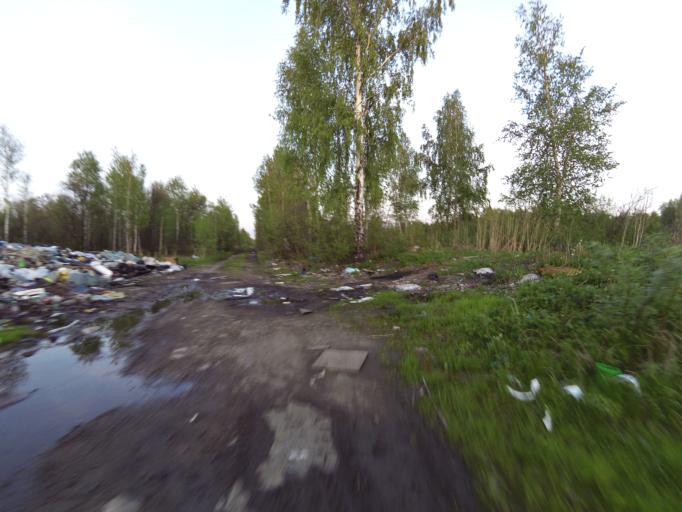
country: RU
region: Sverdlovsk
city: Shirokaya Rechka
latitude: 56.8407
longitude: 60.5047
